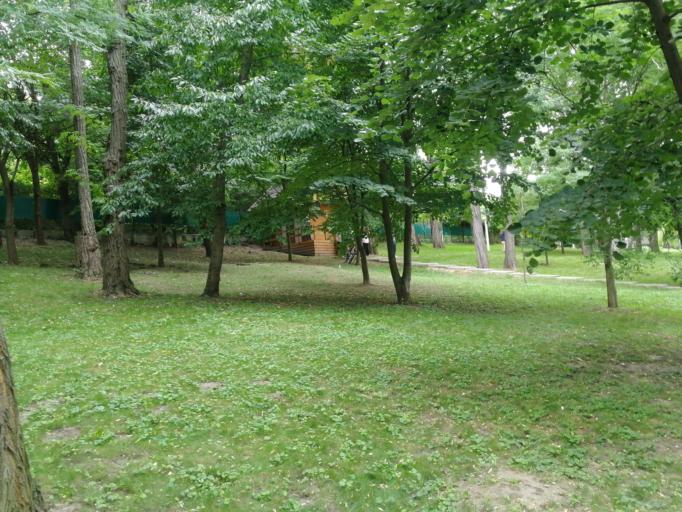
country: MD
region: Chisinau
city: Vatra
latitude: 47.1007
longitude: 28.7051
